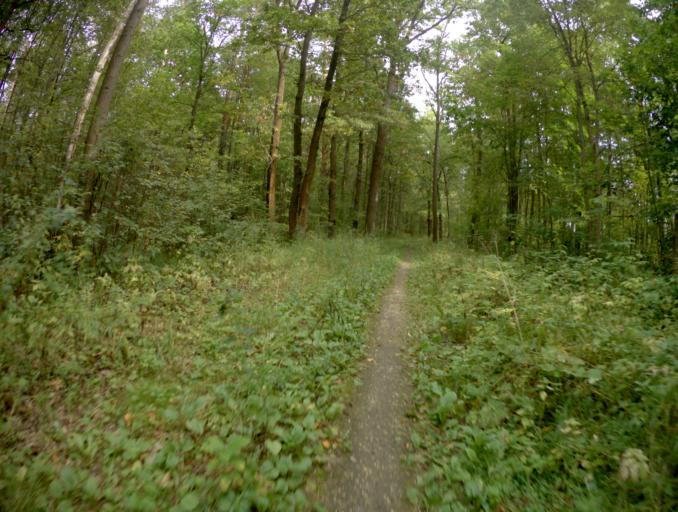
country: RU
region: Vladimir
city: Raduzhnyy
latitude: 56.0511
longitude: 40.2926
